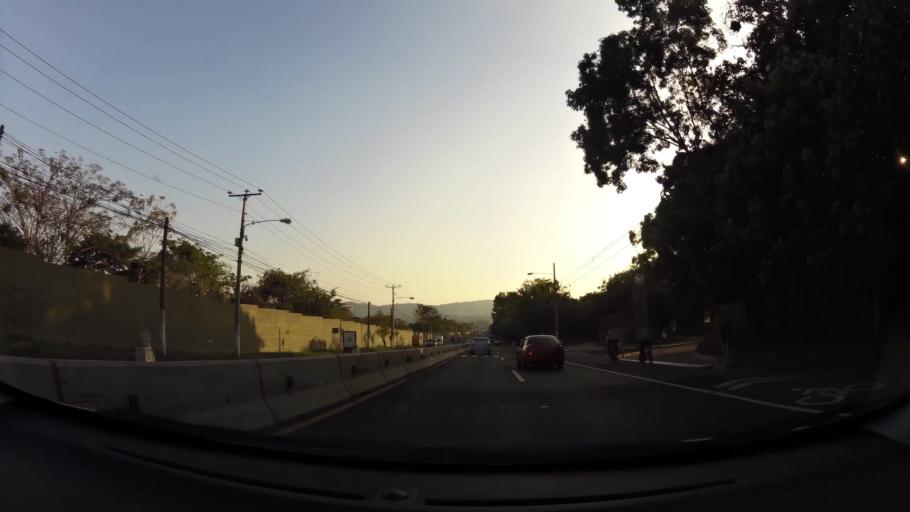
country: SV
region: La Libertad
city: Antiguo Cuscatlan
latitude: 13.6947
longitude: -89.2502
